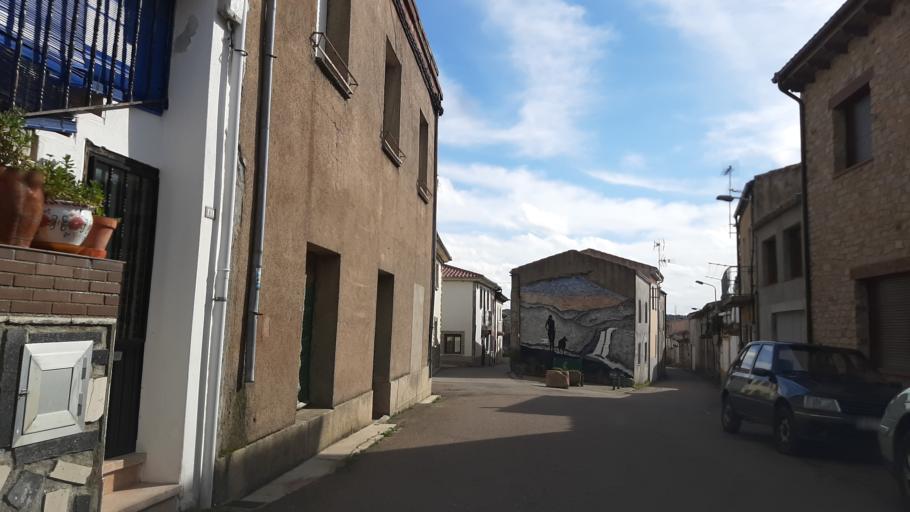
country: ES
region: Castille and Leon
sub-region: Provincia de Salamanca
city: Villarino de los Aires
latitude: 41.2393
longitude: -6.5230
